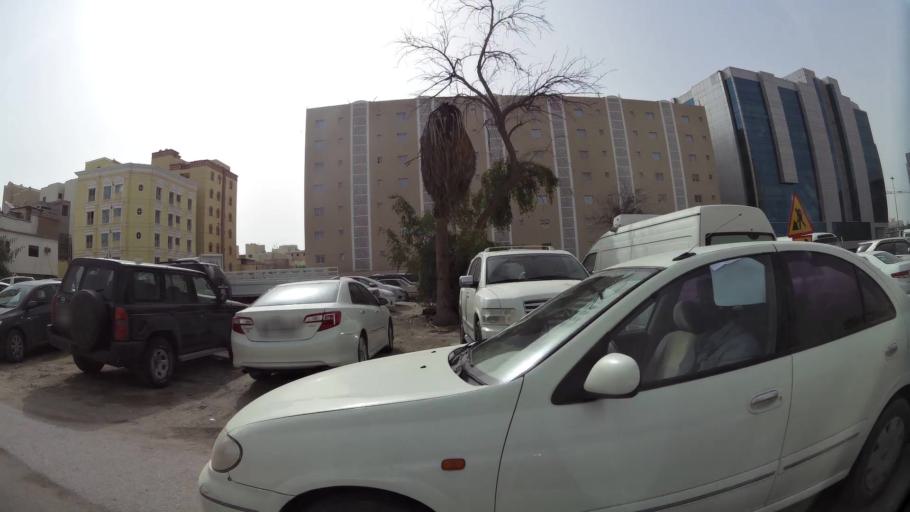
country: QA
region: Baladiyat ad Dawhah
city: Doha
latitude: 25.2749
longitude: 51.5433
